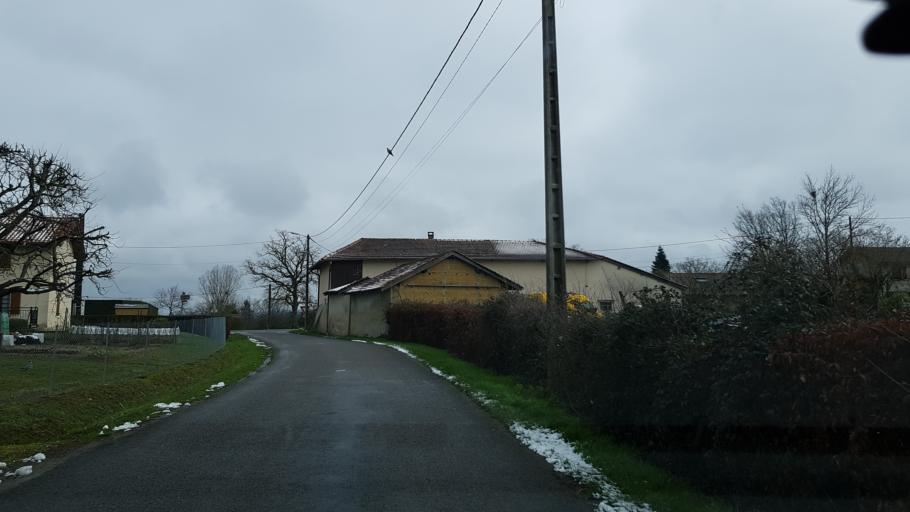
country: FR
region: Rhone-Alpes
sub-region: Departement de l'Ain
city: Saint-Denis-les-Bourg
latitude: 46.1865
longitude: 5.1640
